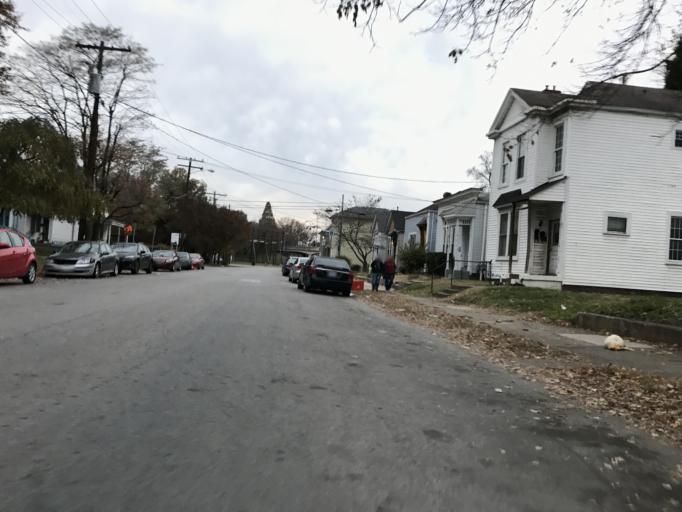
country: US
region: Kentucky
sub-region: Jefferson County
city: Louisville
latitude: 38.2308
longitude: -85.7487
